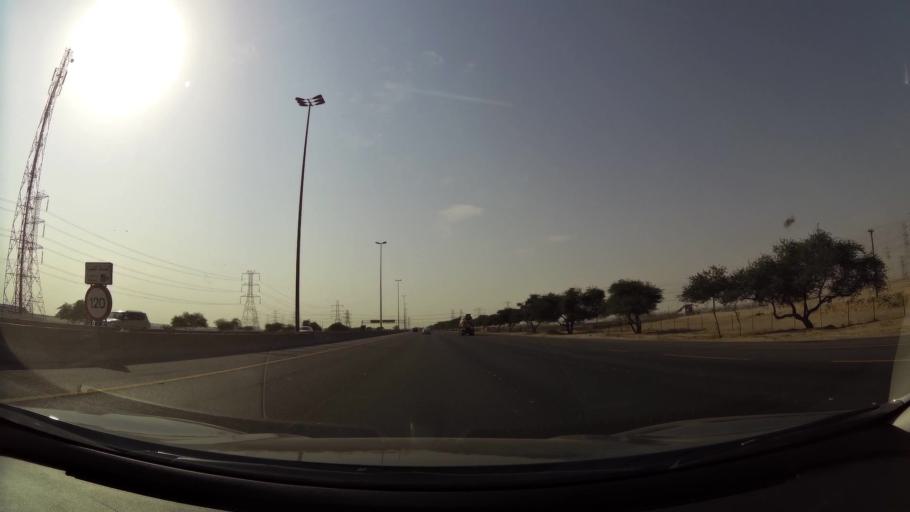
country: KW
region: Al Ahmadi
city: Al Ahmadi
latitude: 29.0204
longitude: 48.0916
